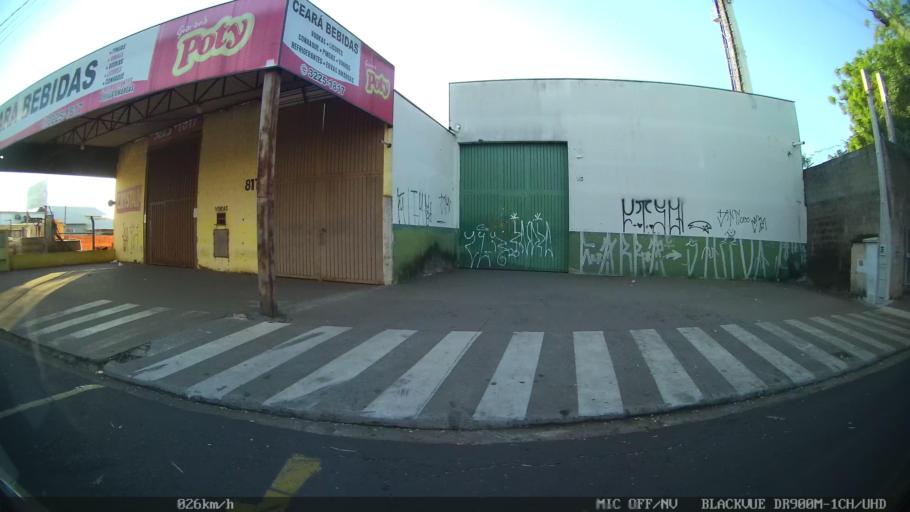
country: BR
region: Sao Paulo
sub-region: Sao Jose Do Rio Preto
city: Sao Jose do Rio Preto
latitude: -20.7795
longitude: -49.3743
